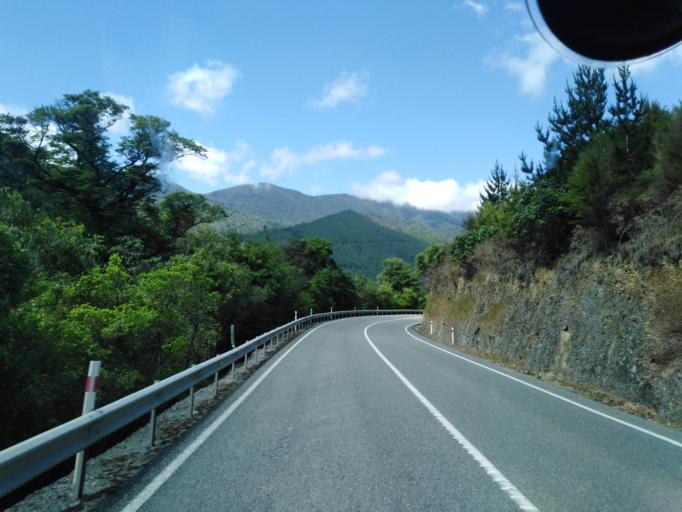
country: NZ
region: Nelson
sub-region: Nelson City
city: Nelson
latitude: -41.2254
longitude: 173.4363
